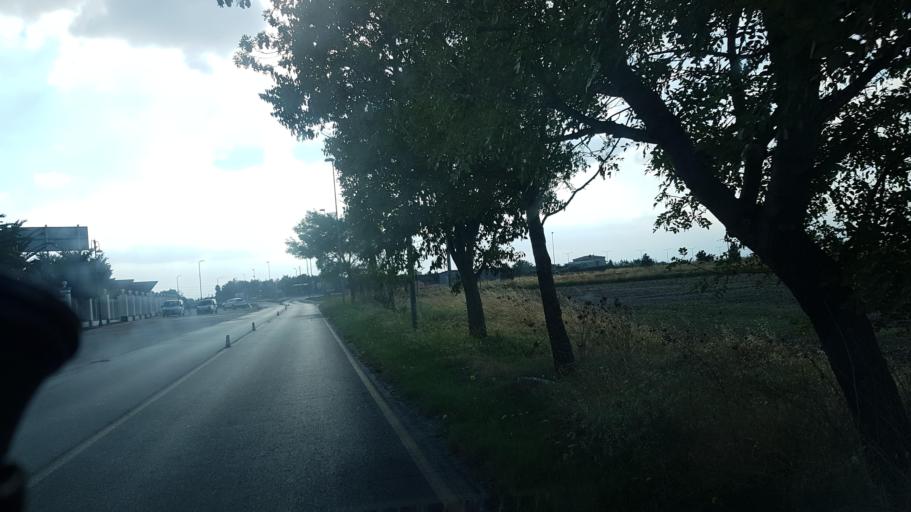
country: IT
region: Apulia
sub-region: Provincia di Foggia
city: Foggia
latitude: 41.4472
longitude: 15.5283
